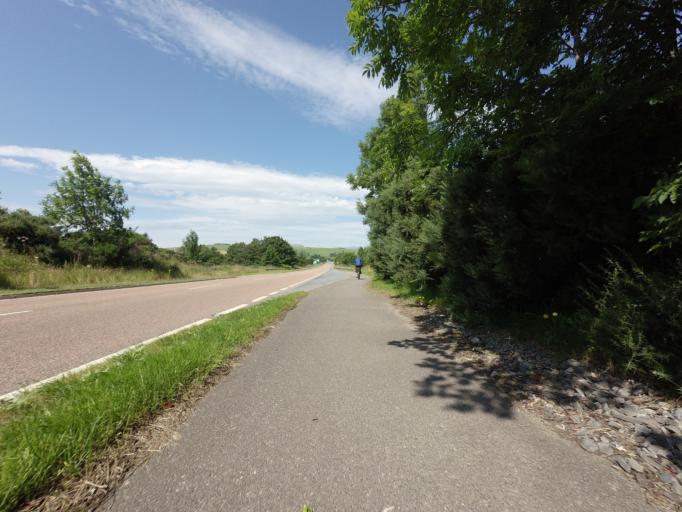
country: GB
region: Scotland
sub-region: Highland
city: Conon Bridge
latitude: 57.5709
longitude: -4.4280
